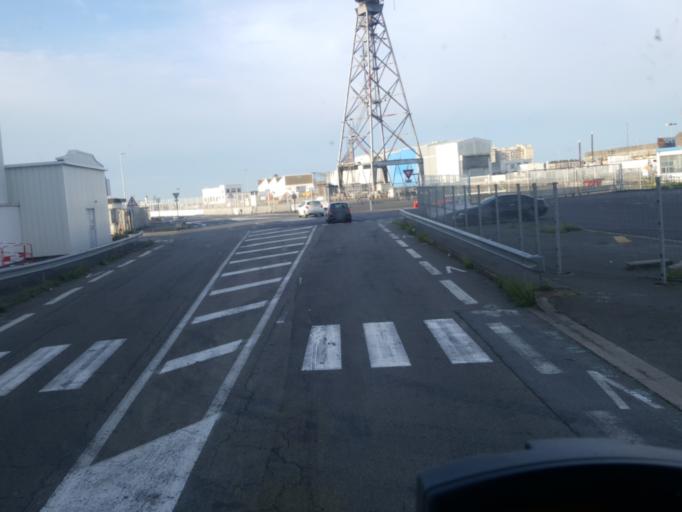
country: FR
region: Pays de la Loire
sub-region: Departement de la Loire-Atlantique
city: Saint-Nazaire
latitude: 47.2796
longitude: -2.1967
